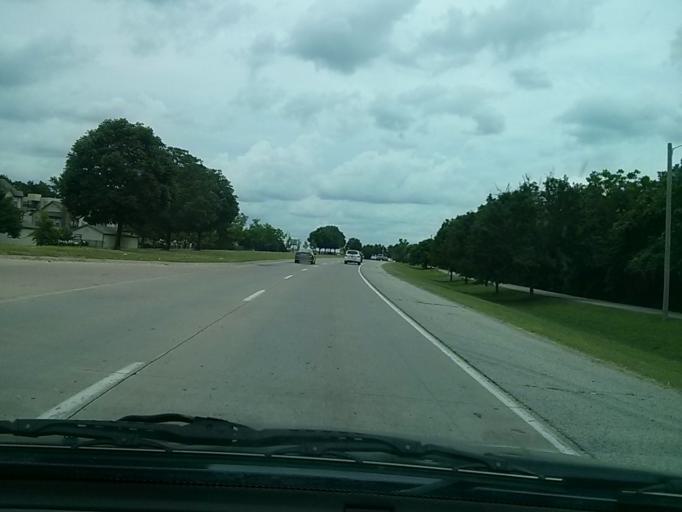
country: US
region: Oklahoma
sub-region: Tulsa County
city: Jenks
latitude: 36.0299
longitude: -95.9527
